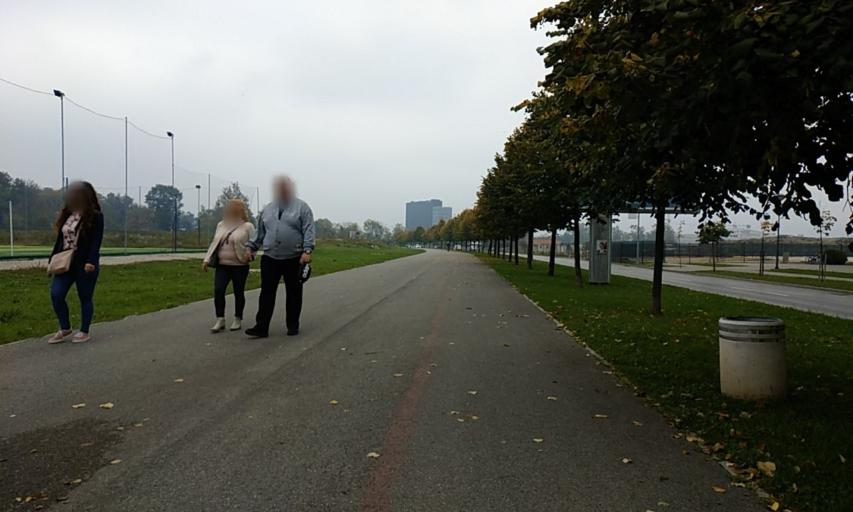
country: BA
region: Republika Srpska
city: Banja Luka
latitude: 44.7765
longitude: 17.2014
